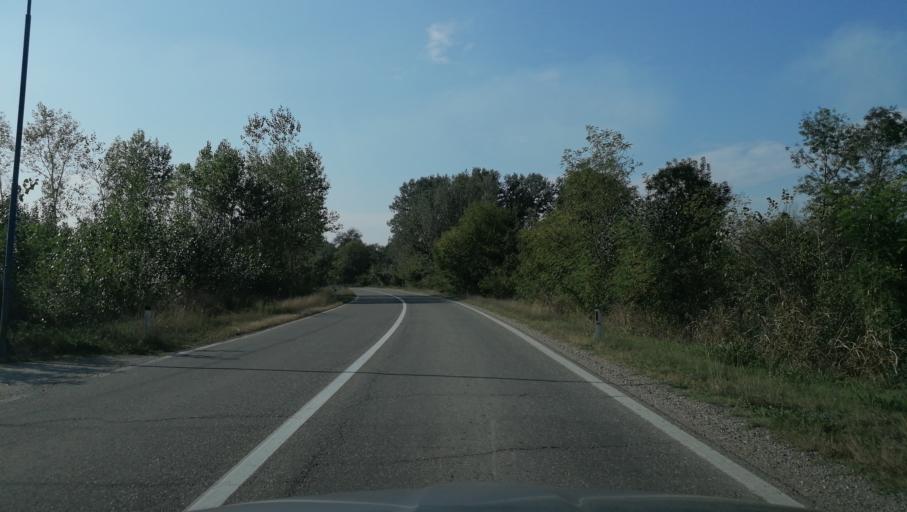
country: BA
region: Republika Srpska
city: Popovi
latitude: 44.7802
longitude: 19.3159
